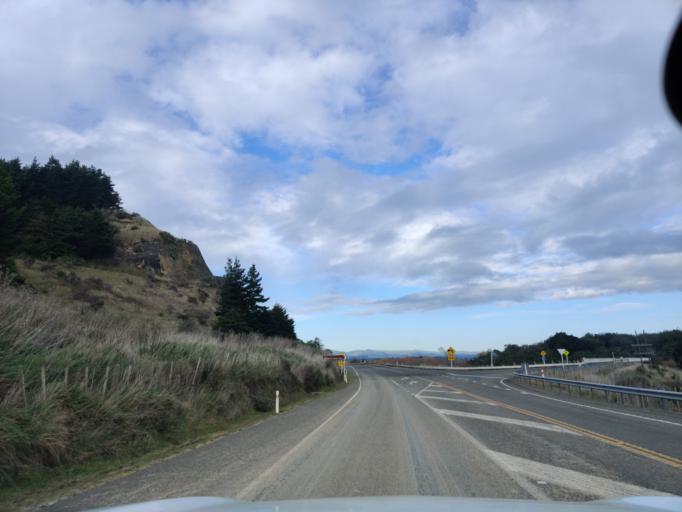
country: NZ
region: Manawatu-Wanganui
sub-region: Palmerston North City
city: Palmerston North
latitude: -40.3361
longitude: 175.8182
